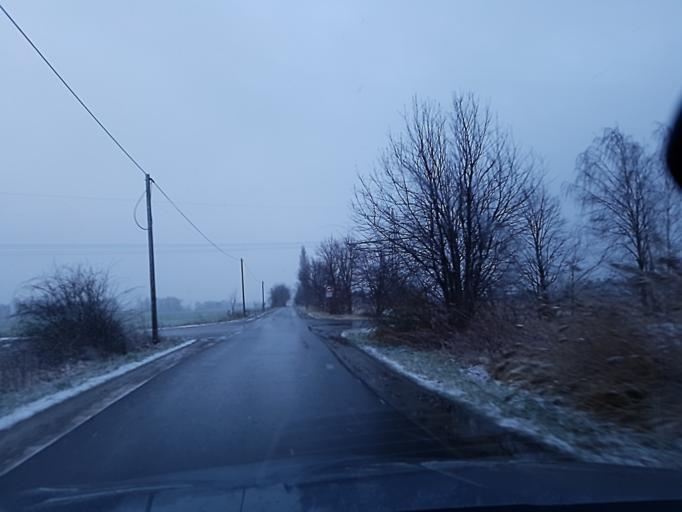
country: DE
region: Brandenburg
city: Elsterwerda
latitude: 51.4441
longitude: 13.5480
